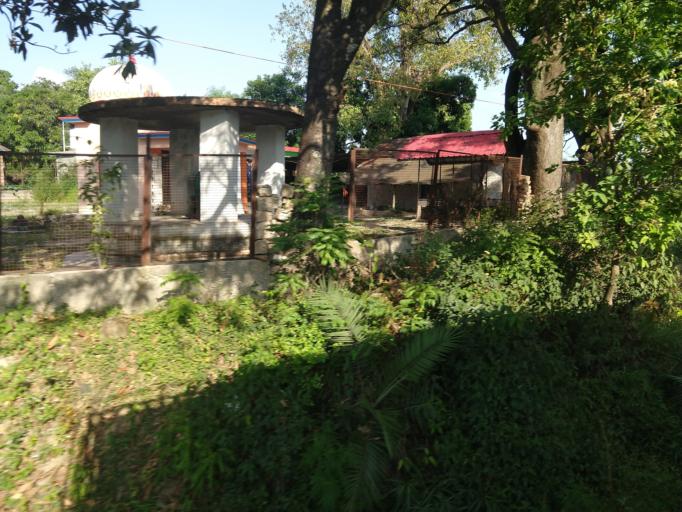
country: IN
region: Himachal Pradesh
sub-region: Chamba
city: Chowari
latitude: 32.3615
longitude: 75.9207
